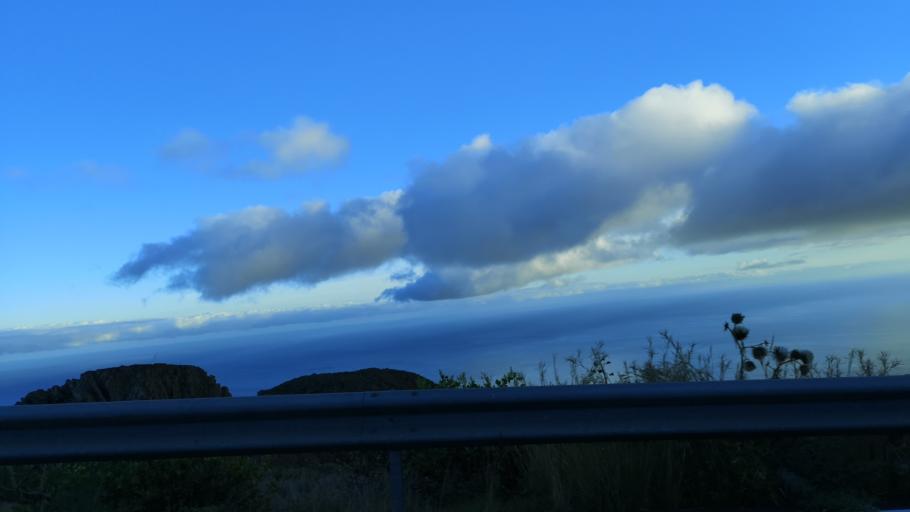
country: ES
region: Canary Islands
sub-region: Provincia de Santa Cruz de Tenerife
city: Alajero
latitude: 28.0565
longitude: -17.2282
